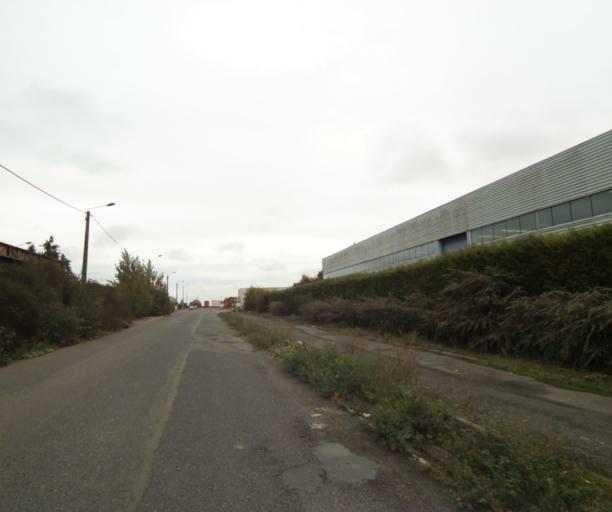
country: FR
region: Centre
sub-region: Departement d'Eure-et-Loir
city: Dreux
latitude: 48.7483
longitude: 1.3679
